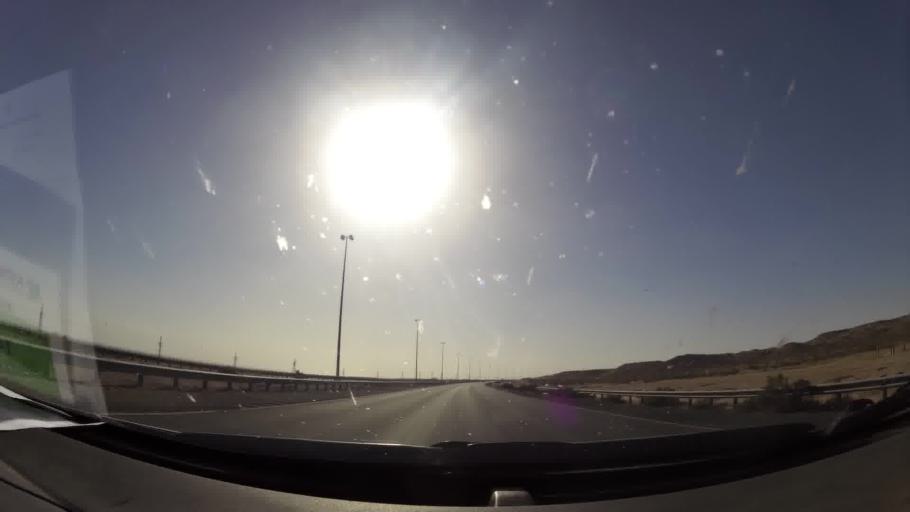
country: KW
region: Al Asimah
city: Kuwait City
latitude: 29.5520
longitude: 47.8764
